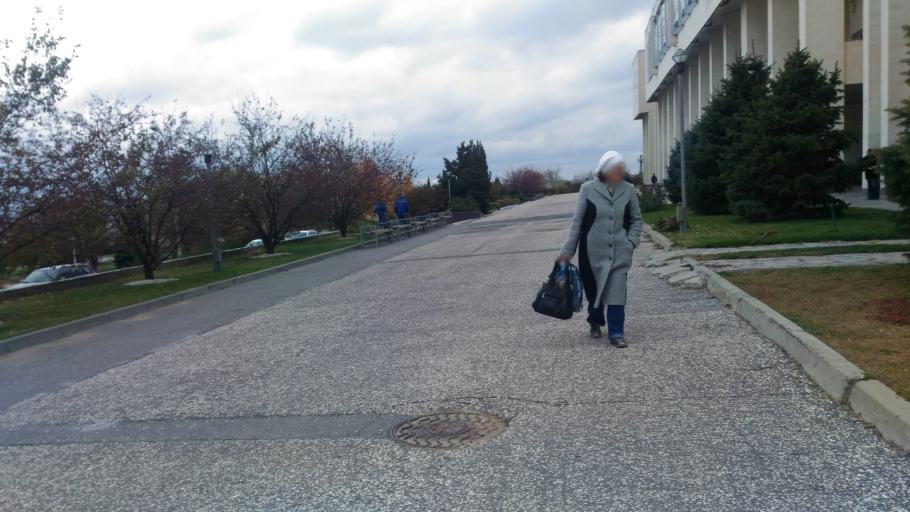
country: RU
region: Volgograd
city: Volgograd
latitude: 48.6423
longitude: 44.4234
